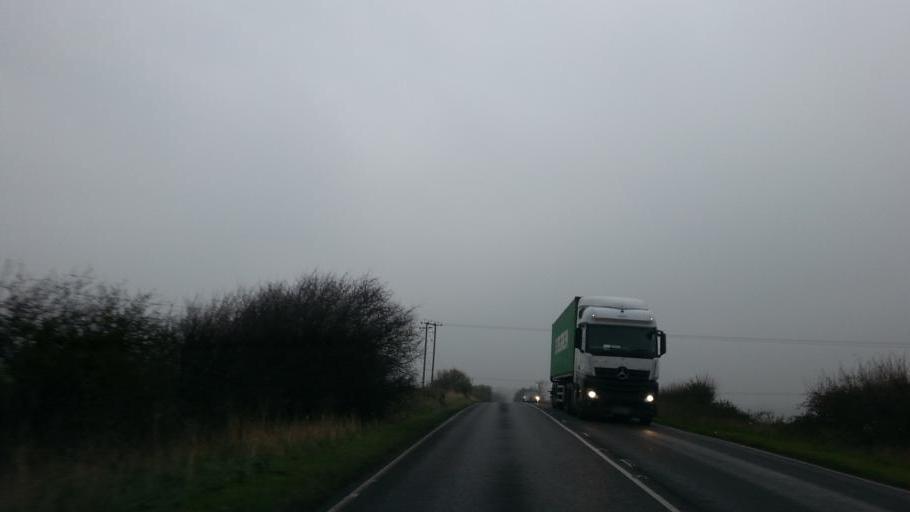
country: GB
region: England
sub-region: Cambridgeshire
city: Papworth Everard
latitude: 52.2640
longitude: -0.1287
